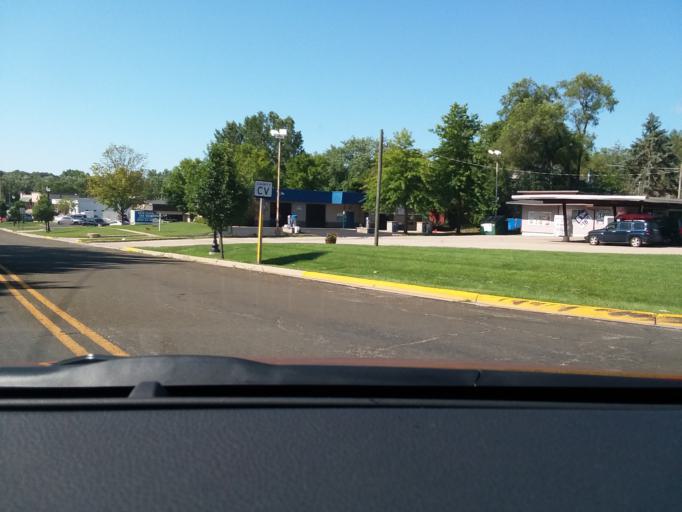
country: US
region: Wisconsin
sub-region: Dane County
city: De Forest
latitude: 43.2526
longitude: -89.3439
